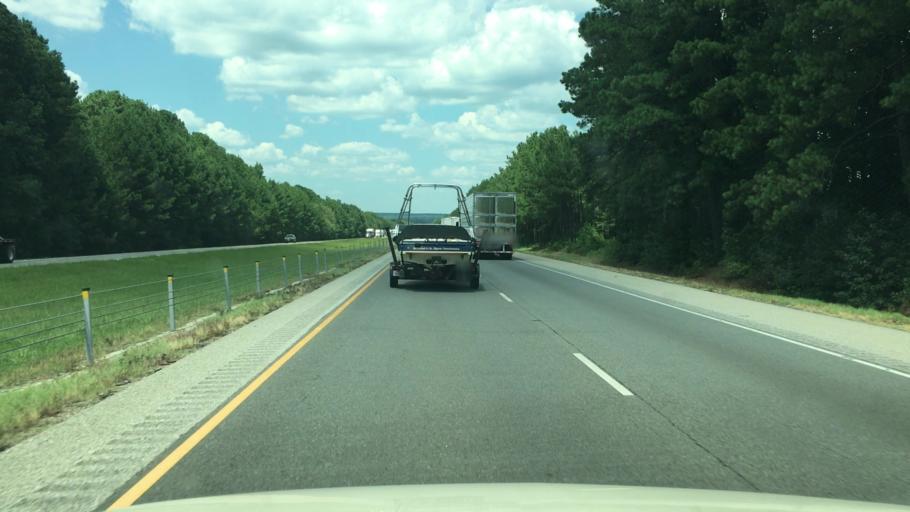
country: US
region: Arkansas
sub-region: Clark County
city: Arkadelphia
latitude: 34.1493
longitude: -93.0787
